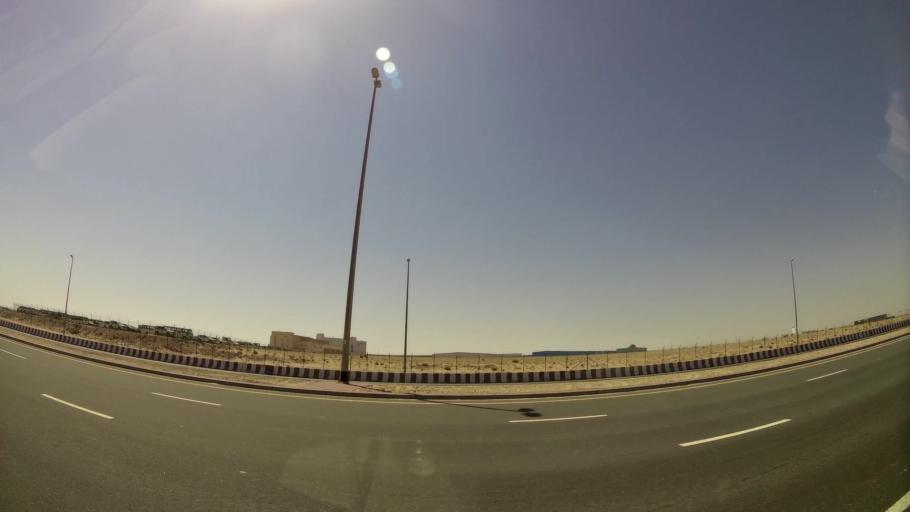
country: AE
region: Dubai
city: Dubai
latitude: 24.9553
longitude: 55.1179
